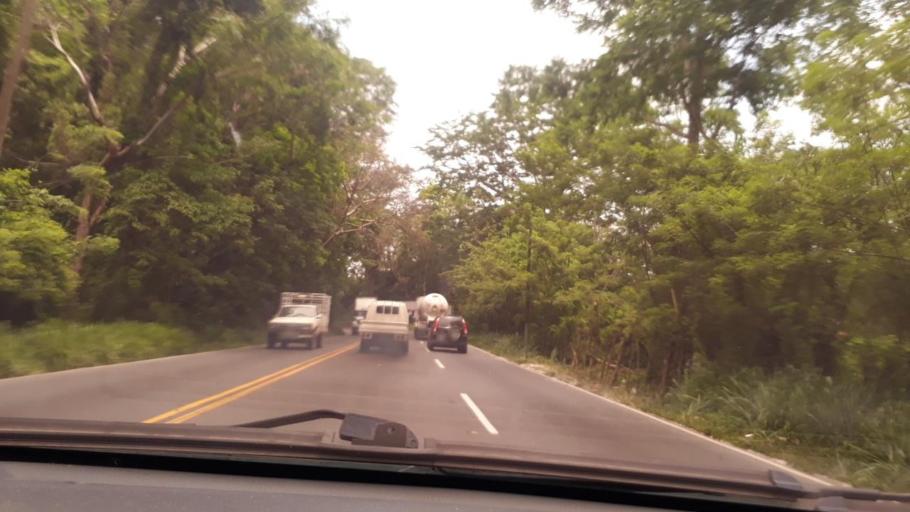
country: GT
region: Izabal
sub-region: Municipio de Los Amates
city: Los Amates
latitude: 15.2460
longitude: -89.1512
